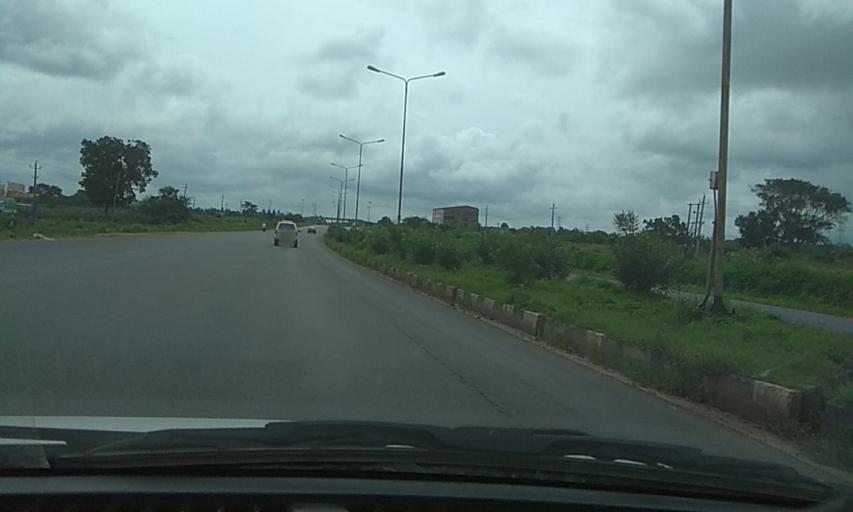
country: IN
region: Karnataka
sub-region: Davanagere
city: Mayakonda
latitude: 14.3774
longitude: 76.1002
